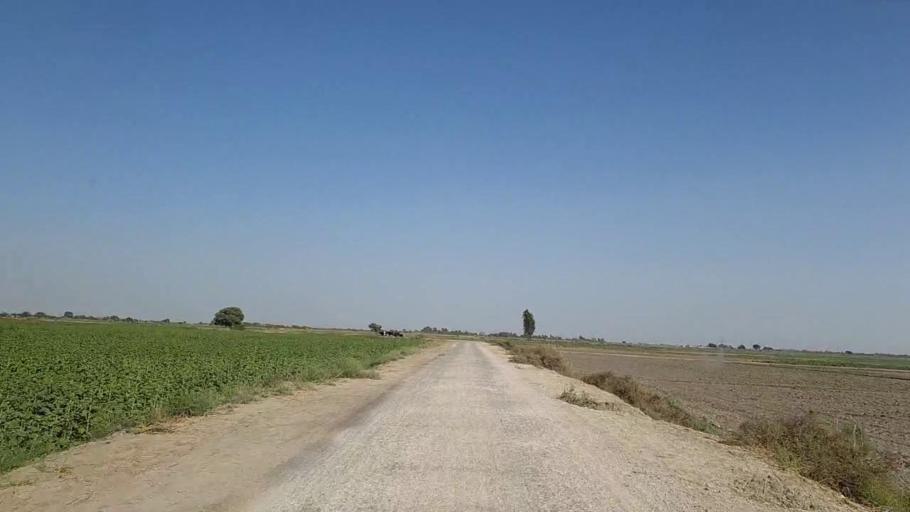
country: PK
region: Sindh
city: Chuhar Jamali
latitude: 24.5250
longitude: 68.1100
